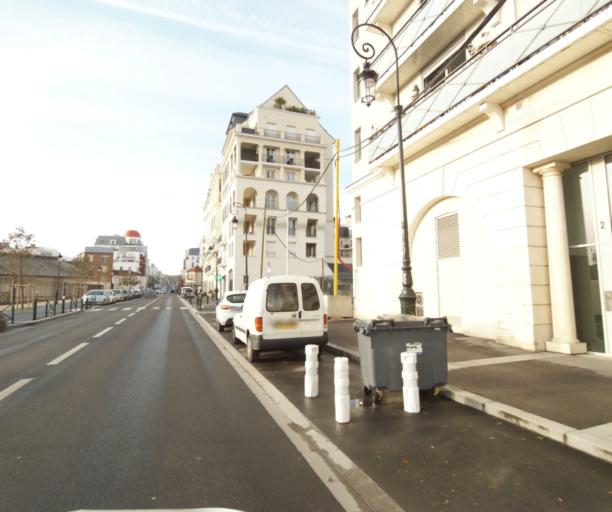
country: FR
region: Ile-de-France
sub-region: Departement des Hauts-de-Seine
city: Puteaux
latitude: 48.8843
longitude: 2.2259
